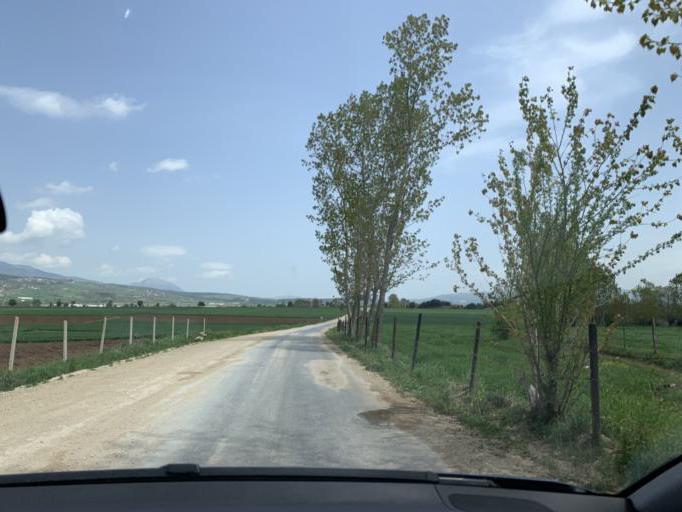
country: TR
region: Bolu
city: Bolu
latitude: 40.7496
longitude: 31.6680
